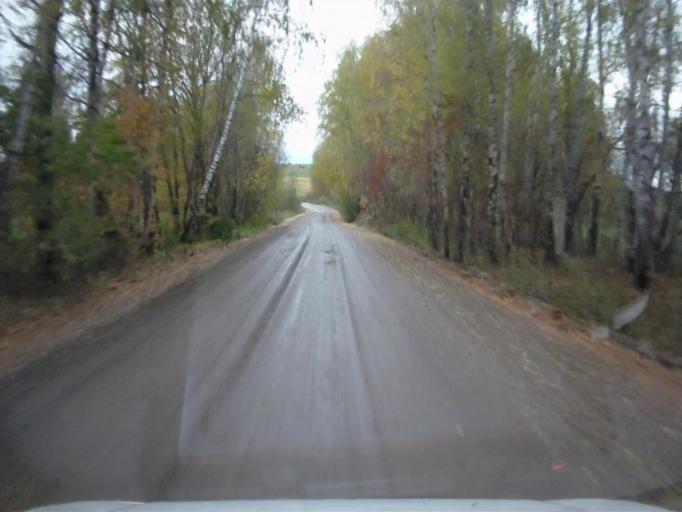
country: RU
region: Sverdlovsk
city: Mikhaylovsk
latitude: 56.1744
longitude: 59.2169
